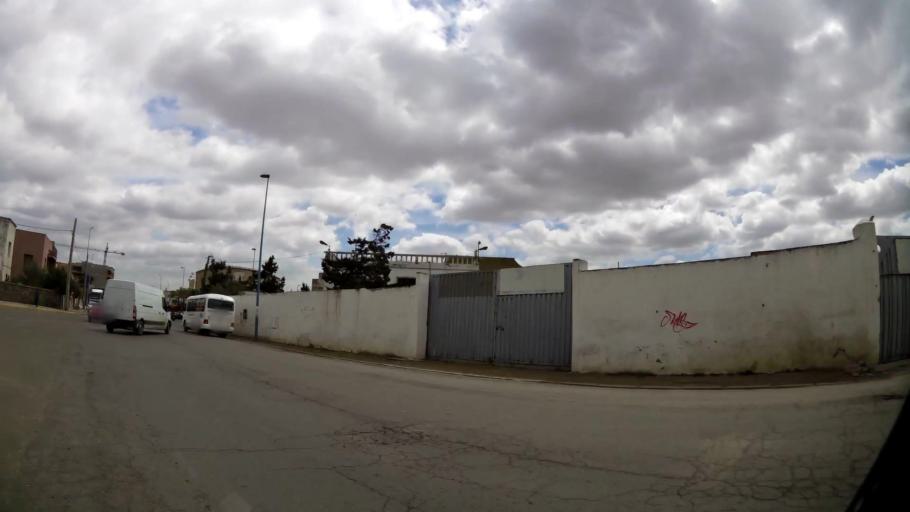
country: MA
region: Grand Casablanca
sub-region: Casablanca
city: Casablanca
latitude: 33.6076
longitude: -7.5480
